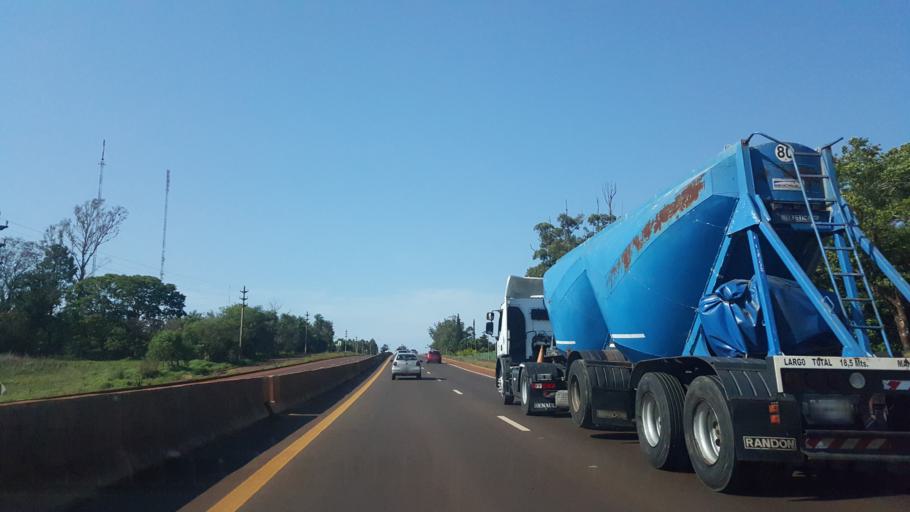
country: AR
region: Misiones
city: Garupa
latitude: -27.4735
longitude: -55.8633
